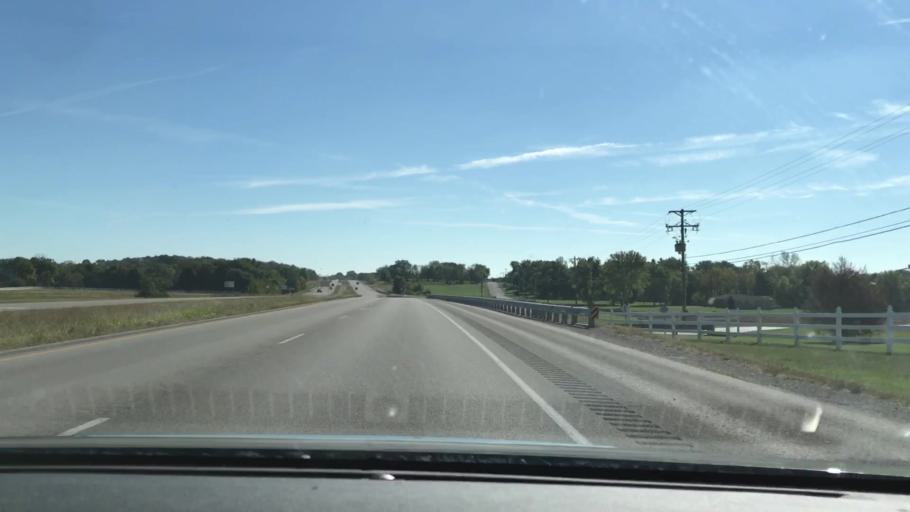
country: US
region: Kentucky
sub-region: Christian County
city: Hopkinsville
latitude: 36.8566
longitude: -87.4221
